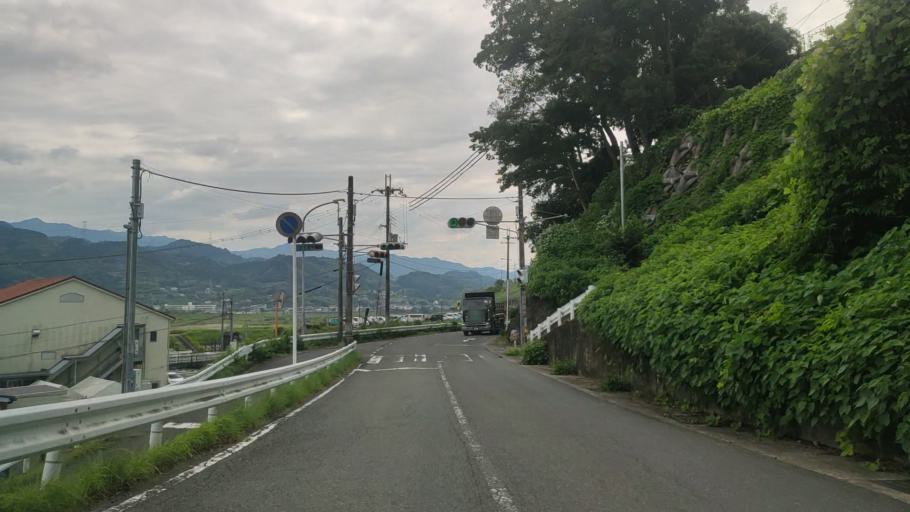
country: JP
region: Wakayama
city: Hashimoto
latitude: 34.3117
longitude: 135.5874
